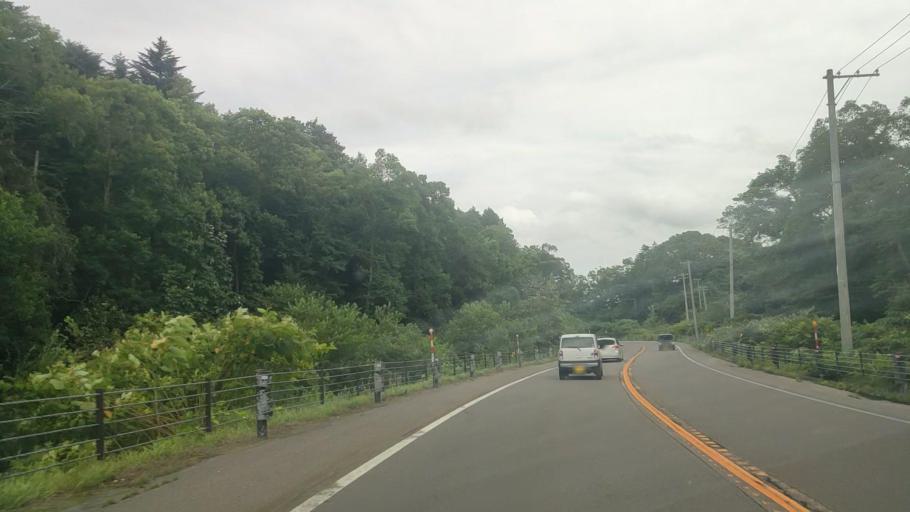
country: JP
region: Hokkaido
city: Nanae
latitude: 41.9680
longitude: 140.6502
